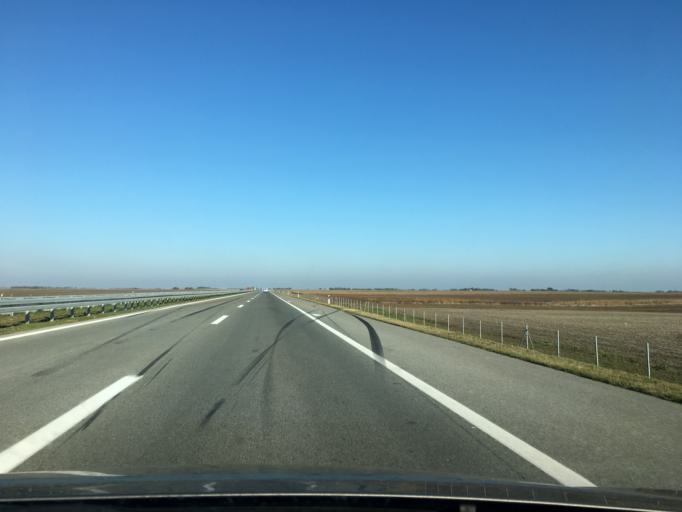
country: RS
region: Autonomna Pokrajina Vojvodina
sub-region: Severnobacki Okrug
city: Mali Igos
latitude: 45.7580
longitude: 19.7017
